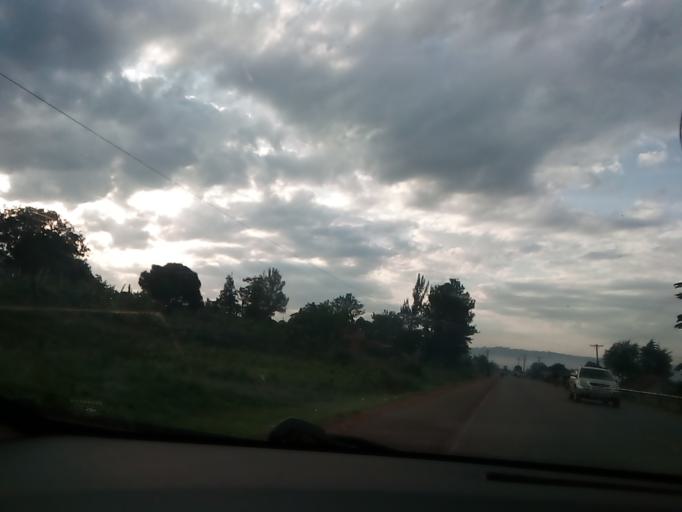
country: UG
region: Central Region
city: Masaka
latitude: -0.3385
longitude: 31.7015
